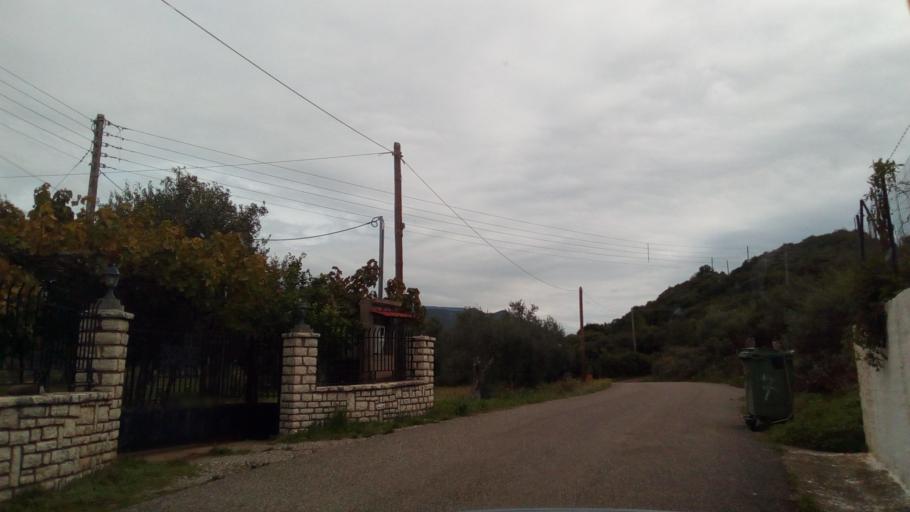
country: GR
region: West Greece
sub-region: Nomos Achaias
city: Kamarai
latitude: 38.4099
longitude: 21.9510
